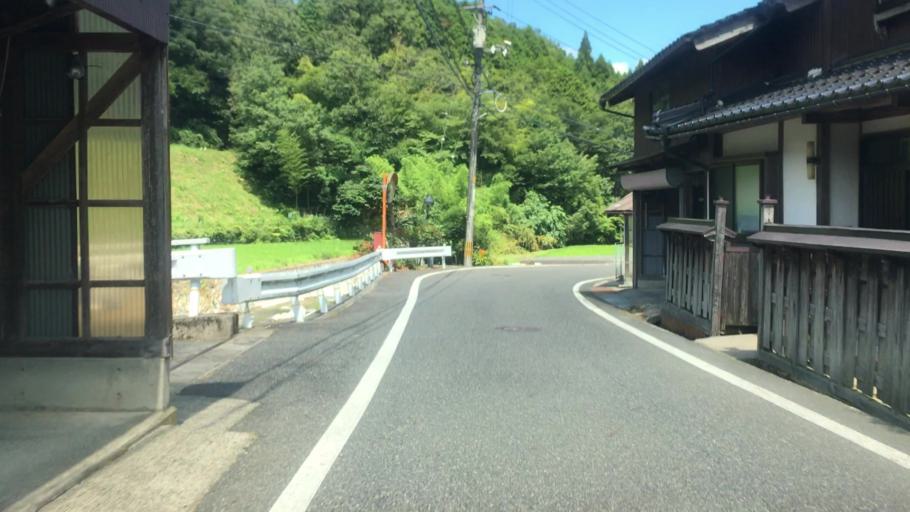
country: JP
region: Okayama
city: Tsuyama
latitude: 35.2130
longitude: 134.2113
